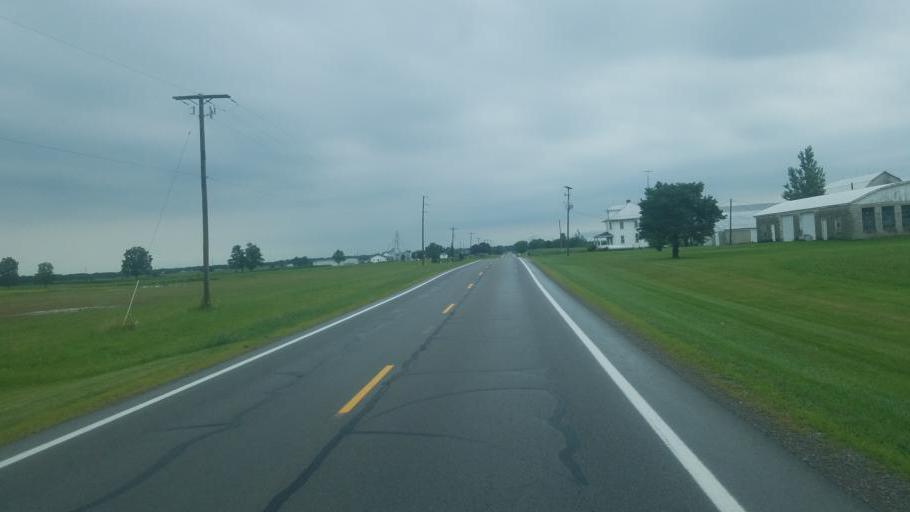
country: US
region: Ohio
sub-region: Hardin County
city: Kenton
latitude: 40.6082
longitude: -83.5953
